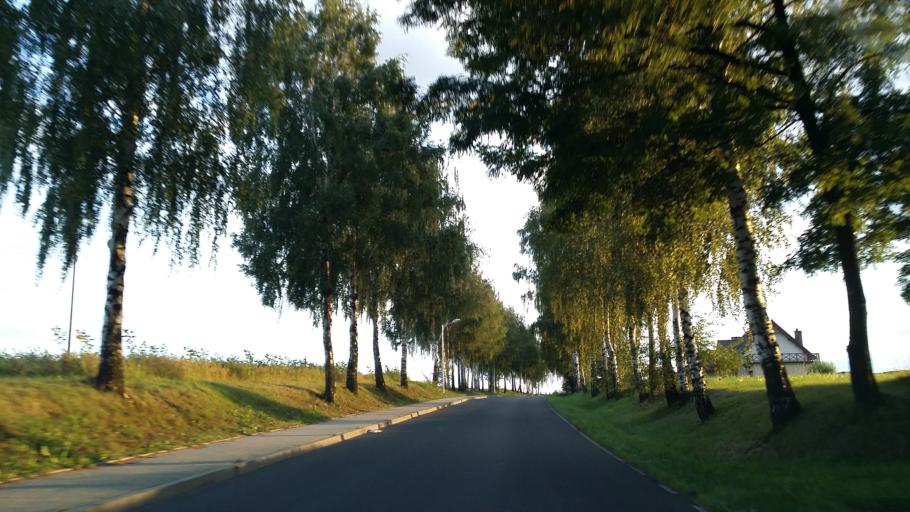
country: PL
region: Lesser Poland Voivodeship
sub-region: Powiat oswiecimski
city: Malec
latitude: 49.9193
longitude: 19.2441
